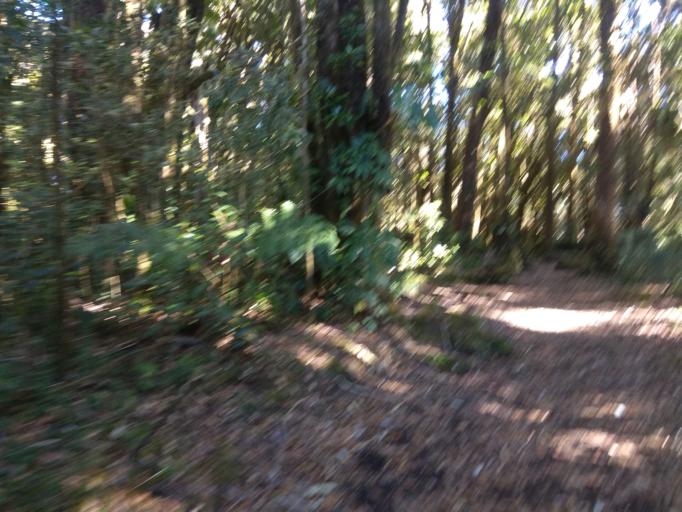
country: CR
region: Heredia
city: Santo Domingo
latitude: 10.1328
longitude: -84.1162
